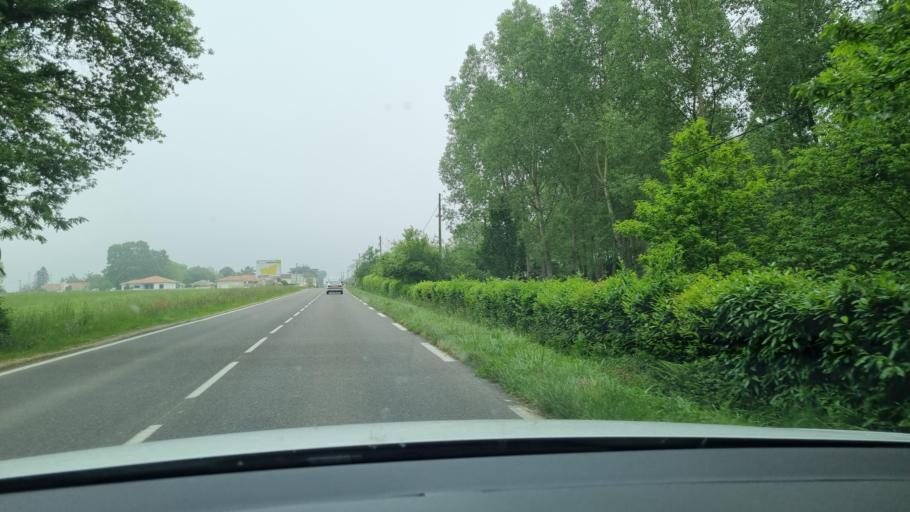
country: FR
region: Aquitaine
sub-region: Departement des Landes
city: Hagetmau
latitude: 43.6431
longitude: -0.6087
